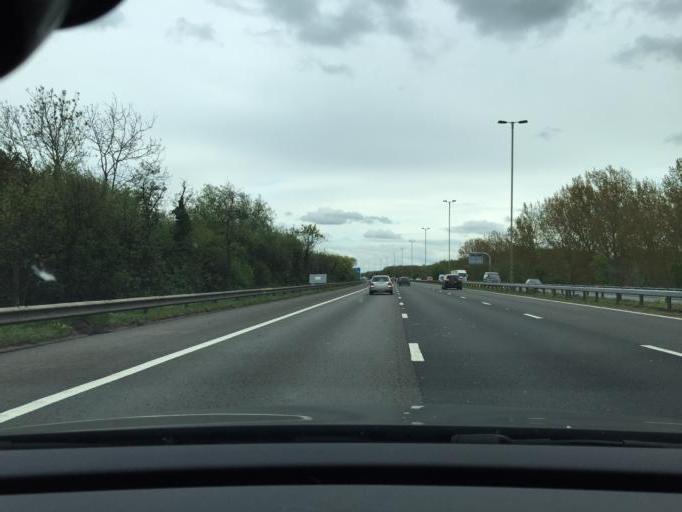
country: GB
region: England
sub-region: West Berkshire
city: Calcot
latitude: 51.4312
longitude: -1.0488
